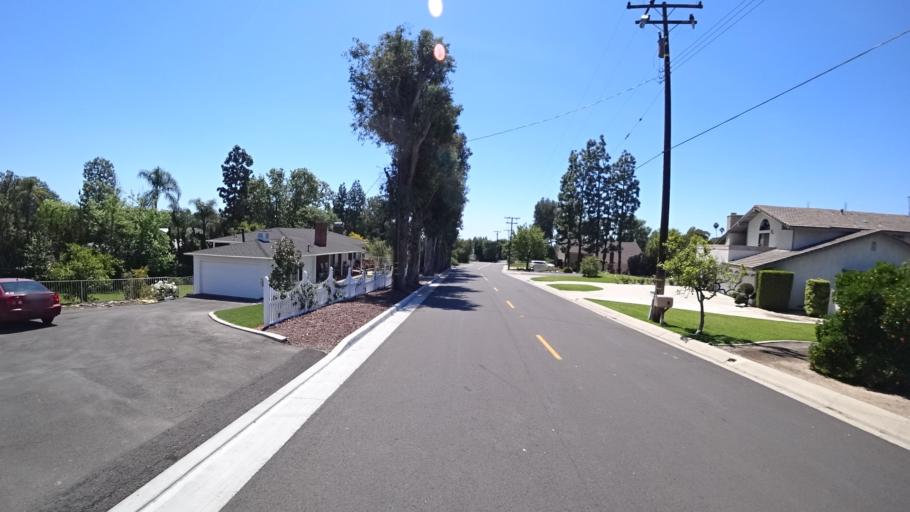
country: US
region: California
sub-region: Orange County
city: Villa Park
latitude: 33.8282
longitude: -117.7984
